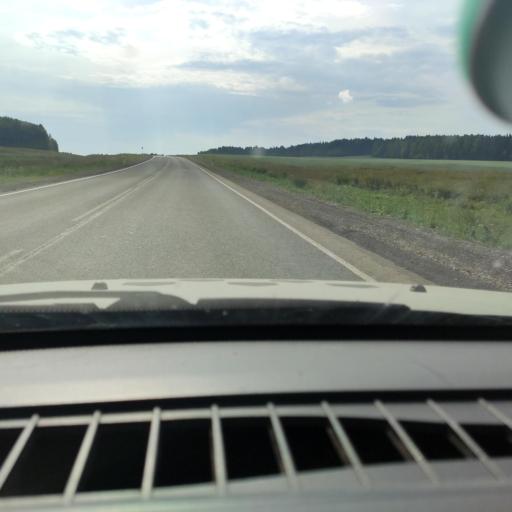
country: RU
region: Perm
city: Siva
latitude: 58.4051
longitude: 54.4796
